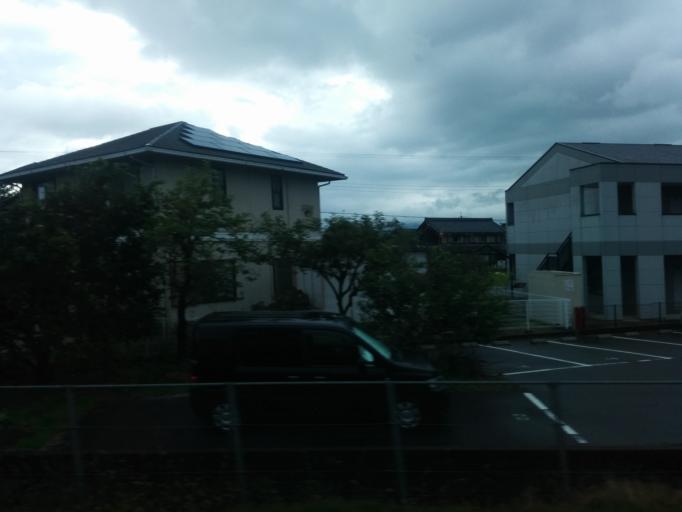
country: JP
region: Shiga Prefecture
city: Moriyama
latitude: 35.0416
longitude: 135.9849
